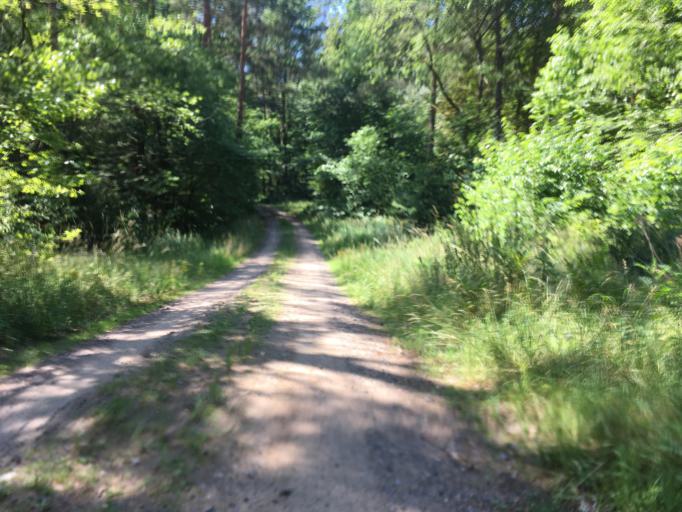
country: DE
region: Brandenburg
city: Marienwerder
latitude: 52.9220
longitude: 13.6480
